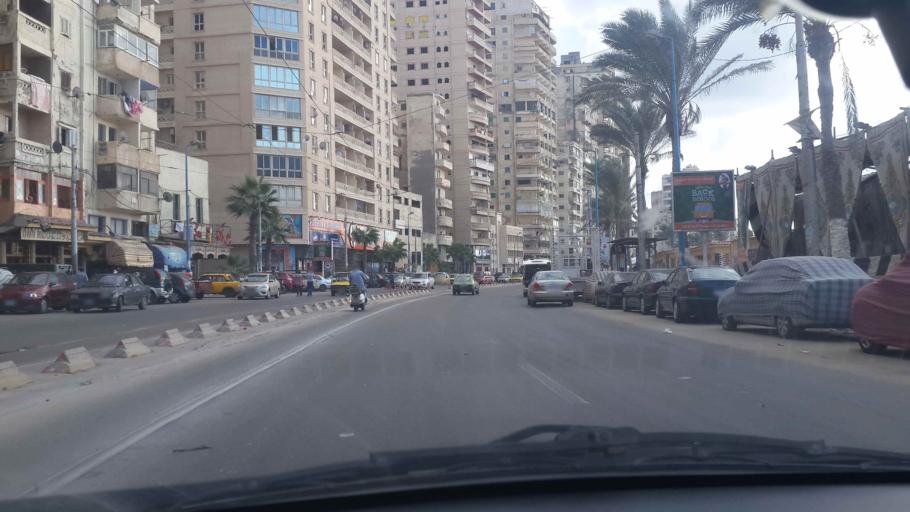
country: EG
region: Alexandria
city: Alexandria
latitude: 31.2057
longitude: 29.8784
